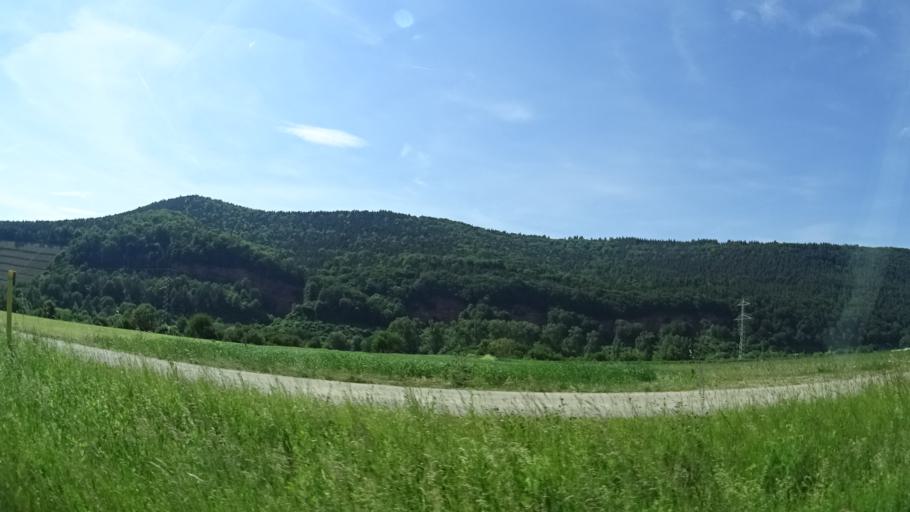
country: DE
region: Bavaria
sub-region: Regierungsbezirk Unterfranken
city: Burgstadt
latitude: 49.7230
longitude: 9.2720
